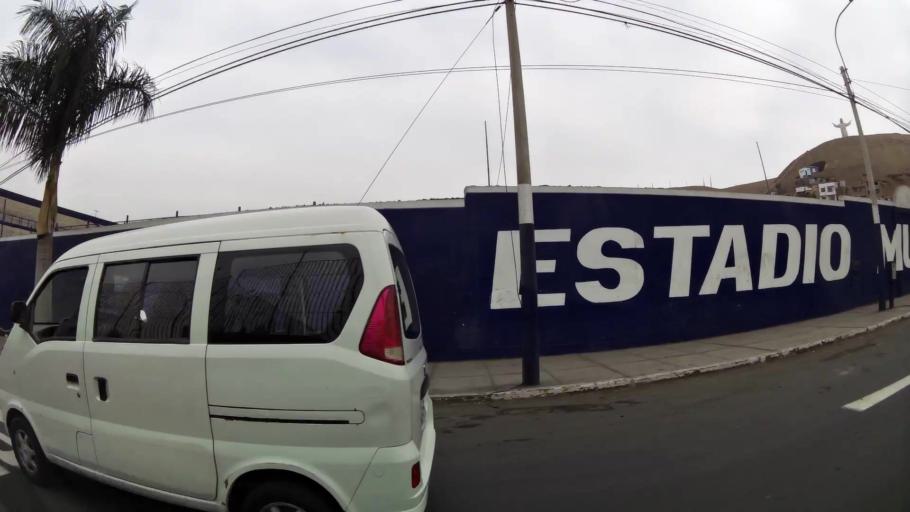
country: PE
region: Lima
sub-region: Lima
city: Surco
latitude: -12.1716
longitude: -77.0279
